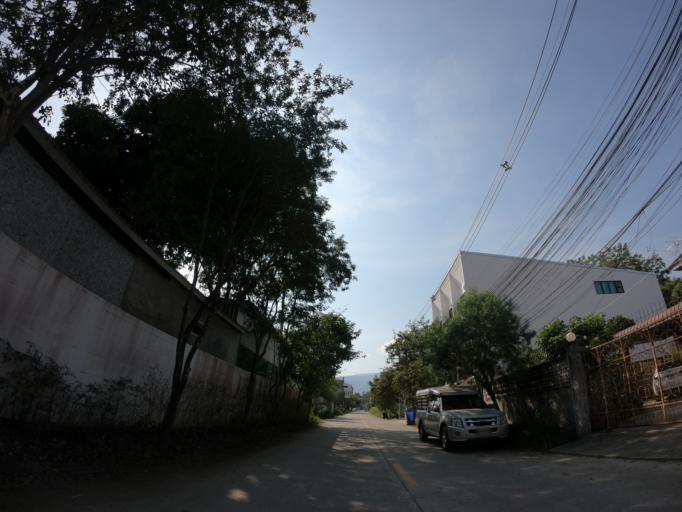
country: TH
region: Chiang Mai
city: Chiang Mai
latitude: 18.8243
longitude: 98.9884
